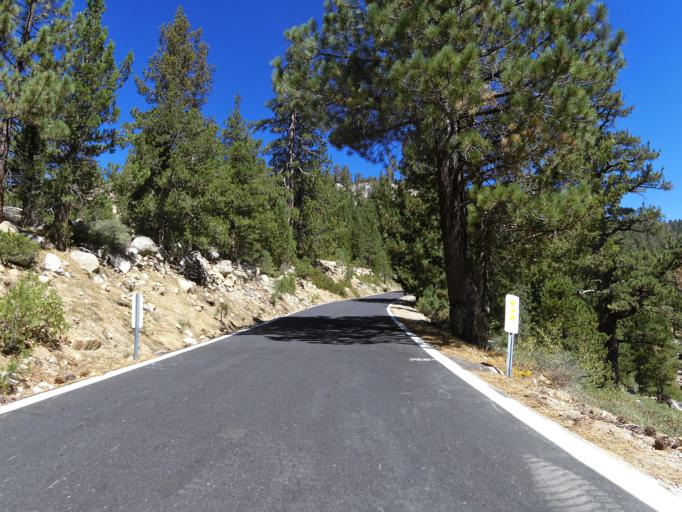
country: US
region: Nevada
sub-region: Douglas County
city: Gardnerville Ranchos
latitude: 38.5430
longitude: -119.8752
